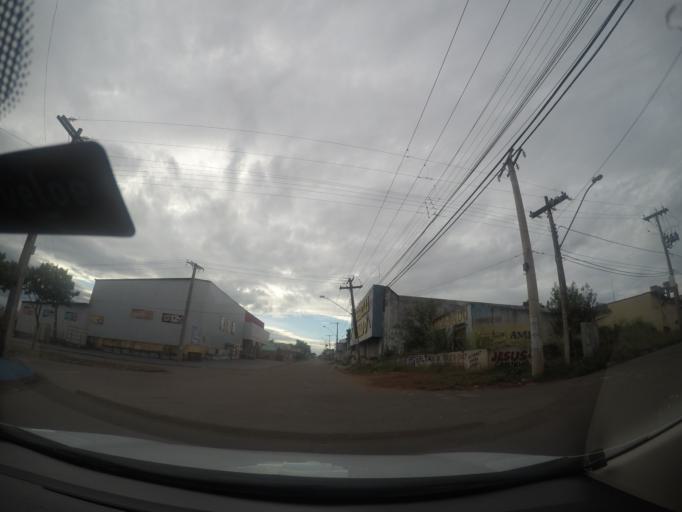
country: BR
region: Goias
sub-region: Goiania
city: Goiania
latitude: -16.6033
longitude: -49.3240
